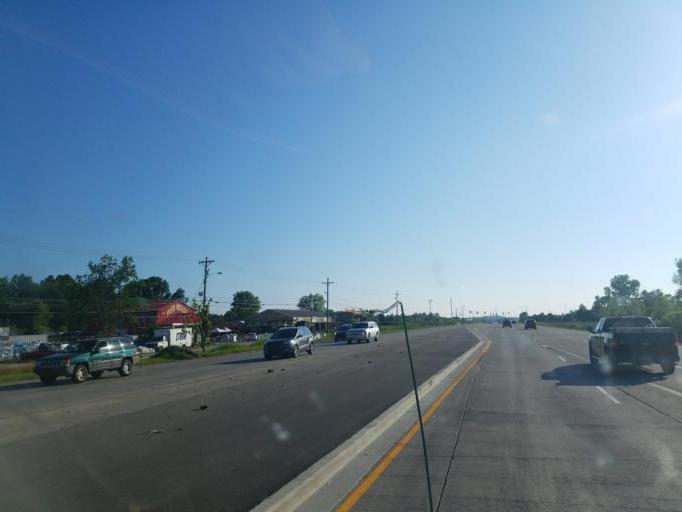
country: US
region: Kentucky
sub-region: Jefferson County
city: Heritage Creek
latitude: 38.1359
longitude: -85.7160
